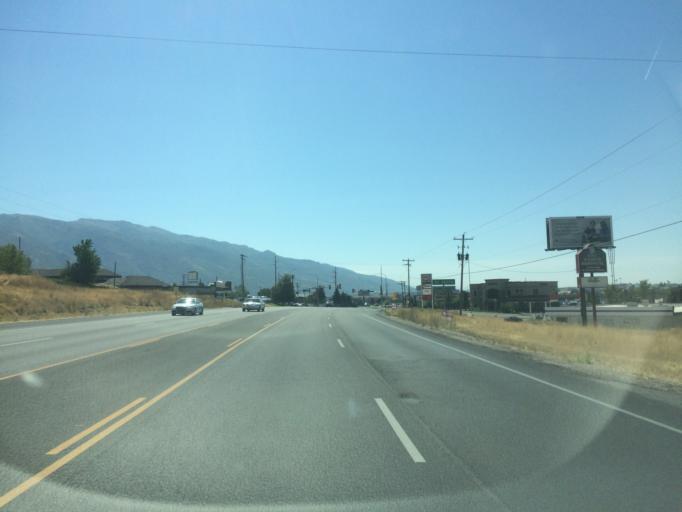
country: US
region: Utah
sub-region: Weber County
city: Uintah
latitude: 41.1635
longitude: -111.9413
